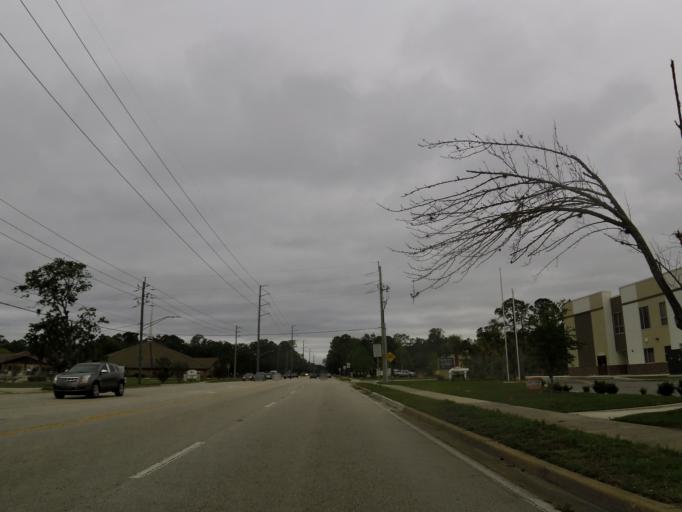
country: US
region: Florida
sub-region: Saint Johns County
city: Fruit Cove
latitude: 30.1765
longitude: -81.6045
